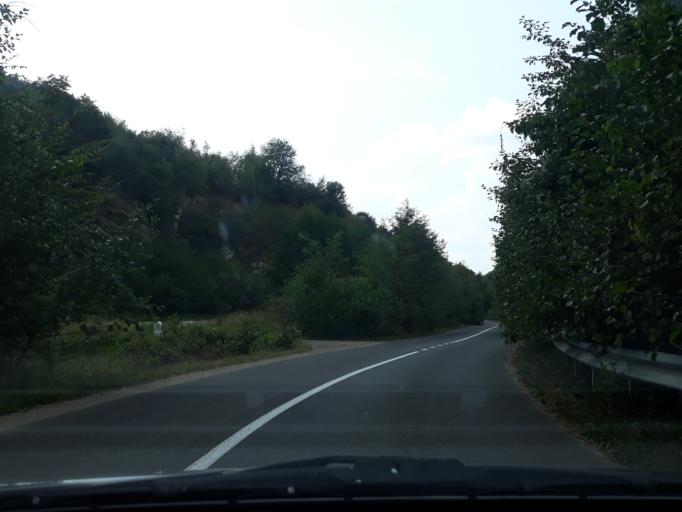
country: RO
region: Bihor
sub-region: Comuna Pietroasa
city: Pietroasa
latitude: 46.5885
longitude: 22.5798
